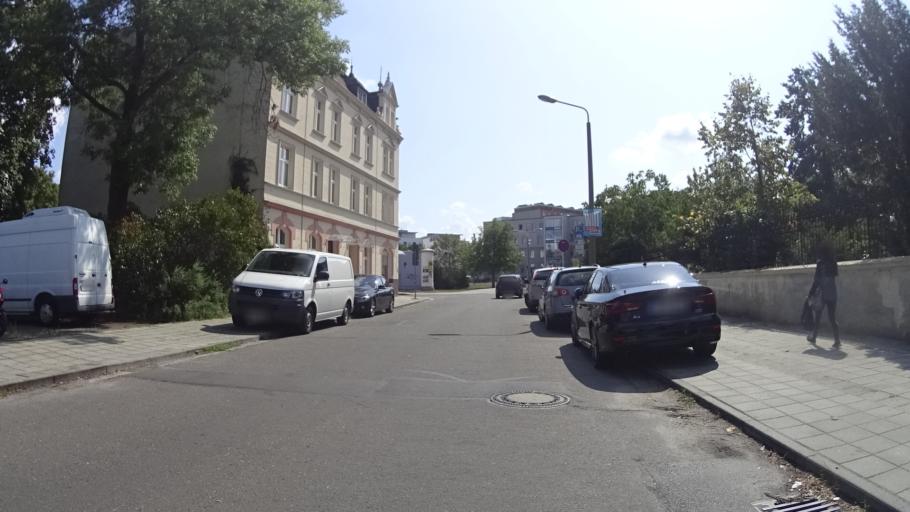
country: DE
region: Brandenburg
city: Cottbus
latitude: 51.7635
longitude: 14.3251
